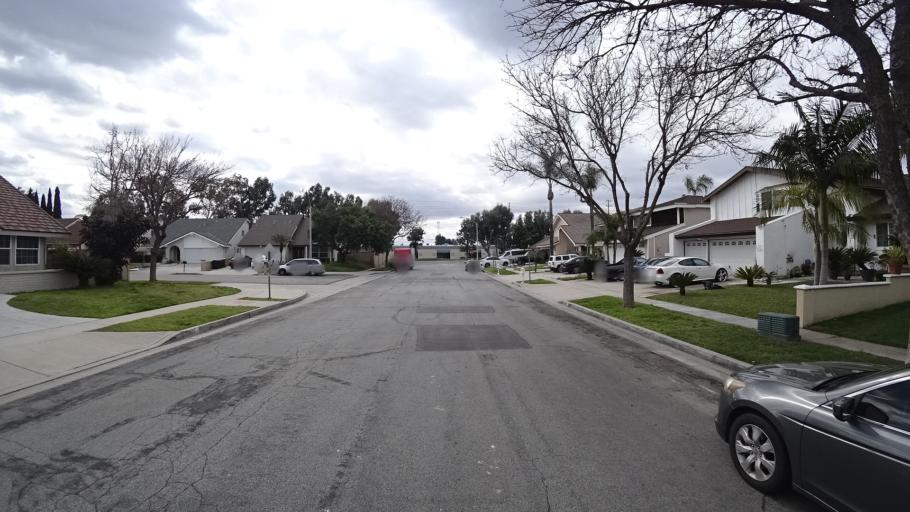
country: US
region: California
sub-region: Orange County
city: Placentia
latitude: 33.8652
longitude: -117.8650
